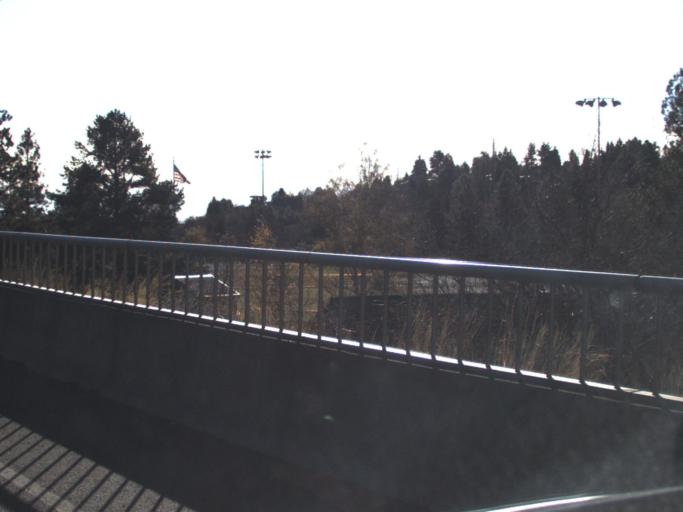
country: US
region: Washington
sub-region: Whitman County
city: Pullman
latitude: 46.7290
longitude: -117.1727
